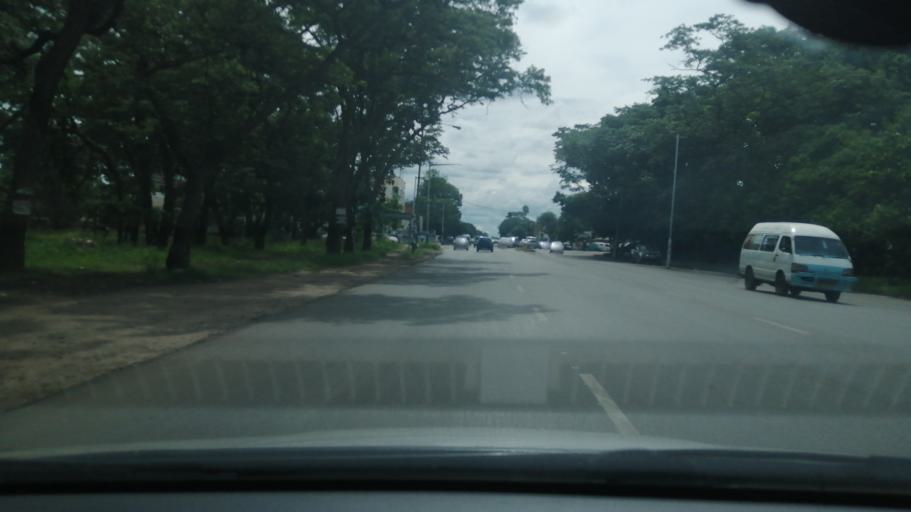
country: ZW
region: Harare
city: Harare
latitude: -17.8194
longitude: 31.0583
